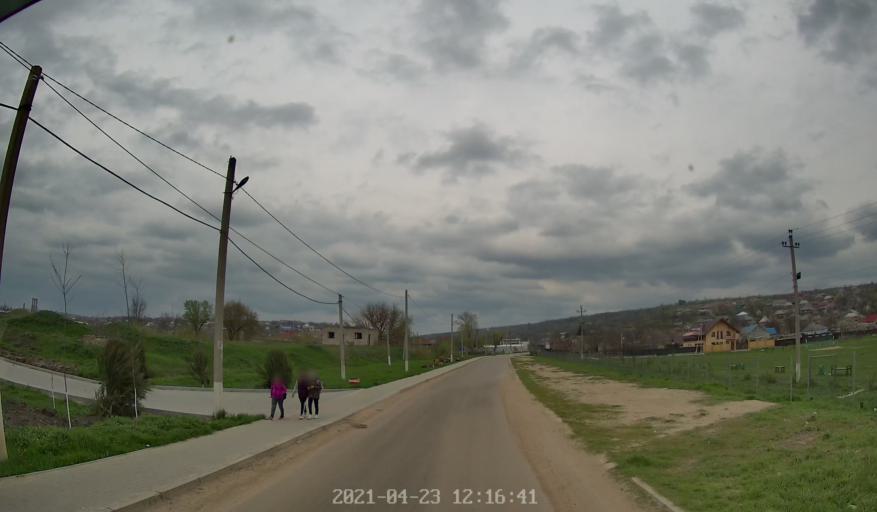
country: MD
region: Chisinau
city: Vadul lui Voda
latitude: 47.1213
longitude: 29.0018
